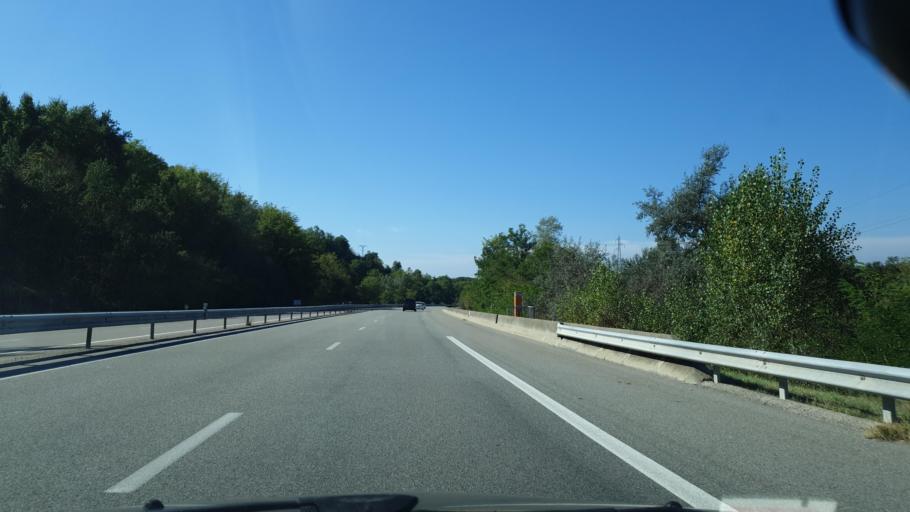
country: FR
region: Rhone-Alpes
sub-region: Departement de l'Isere
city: Saint-Hilaire-du-Rosier
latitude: 45.1064
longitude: 5.2517
